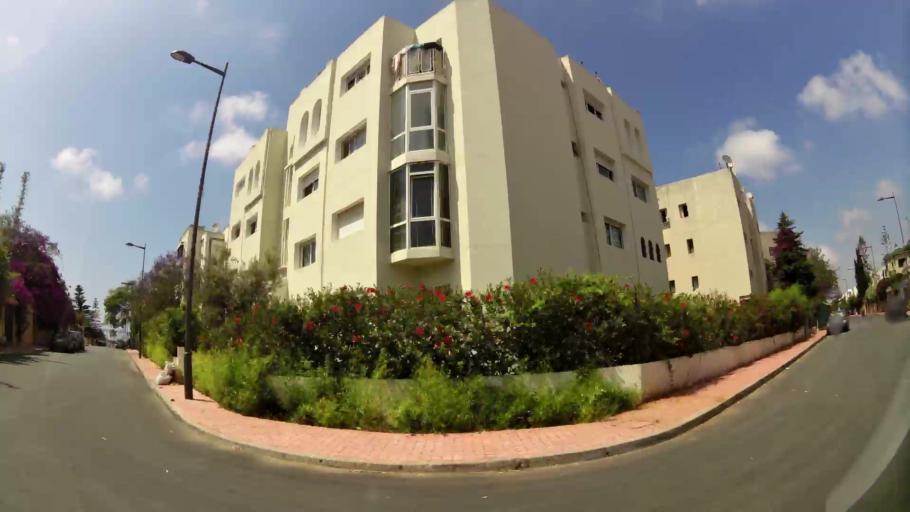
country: MA
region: Rabat-Sale-Zemmour-Zaer
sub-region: Skhirate-Temara
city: Temara
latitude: 33.9558
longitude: -6.8819
